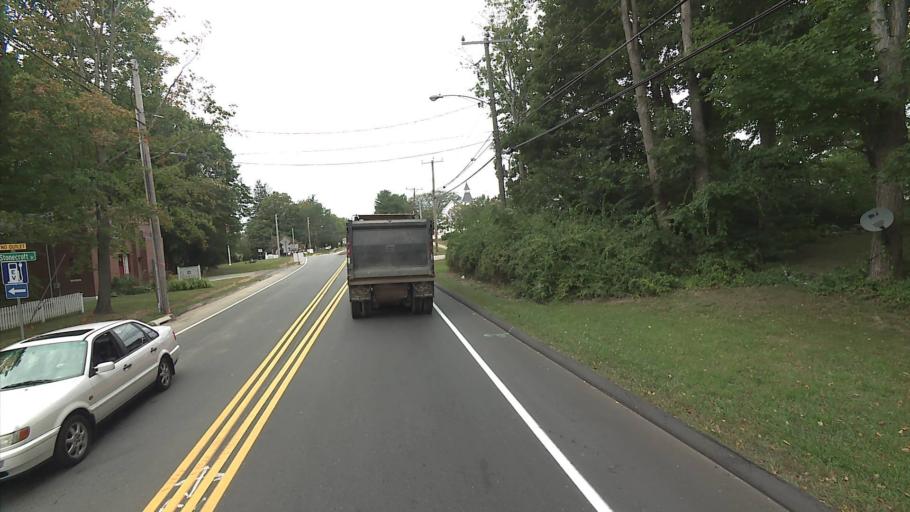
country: US
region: Connecticut
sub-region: Tolland County
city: Hebron
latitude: 41.6572
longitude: -72.3655
